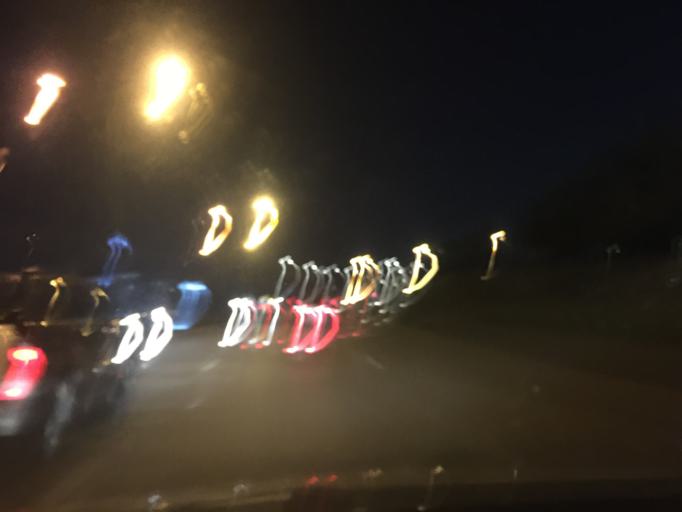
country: JO
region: Amman
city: Wadi as Sir
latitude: 31.9398
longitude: 35.8493
